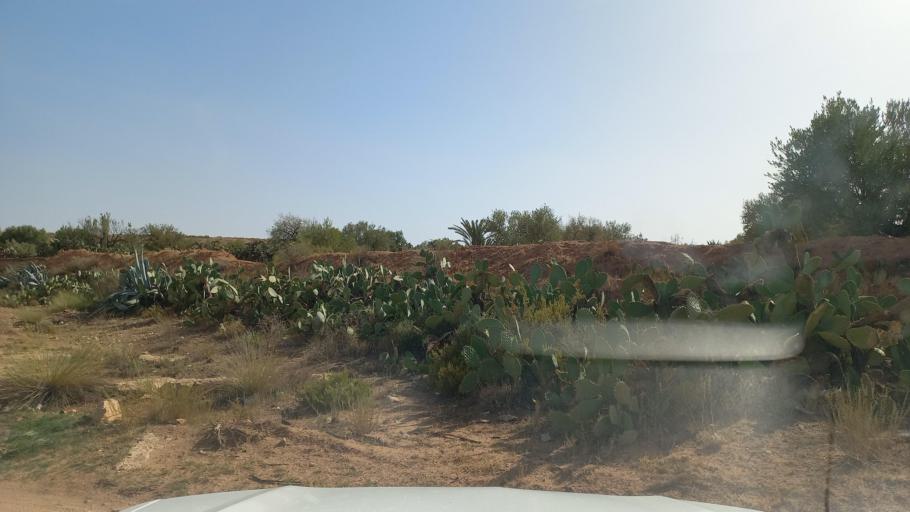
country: TN
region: Al Qasrayn
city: Kasserine
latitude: 35.2011
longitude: 8.9661
